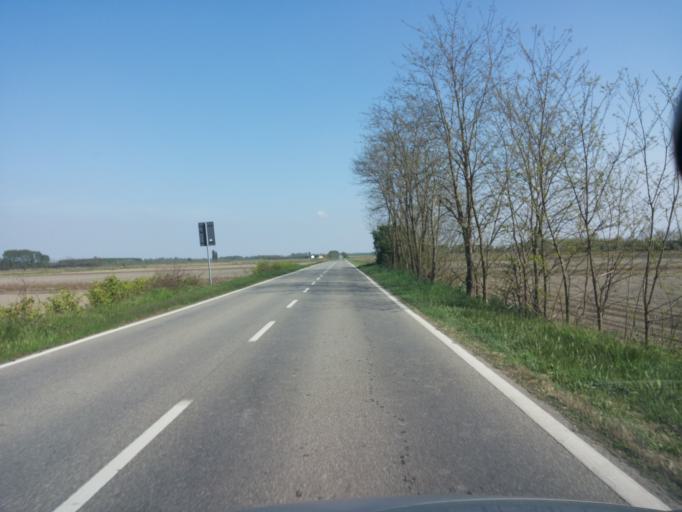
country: IT
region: Piedmont
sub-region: Provincia di Vercelli
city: Caresana
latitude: 45.2141
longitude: 8.5109
